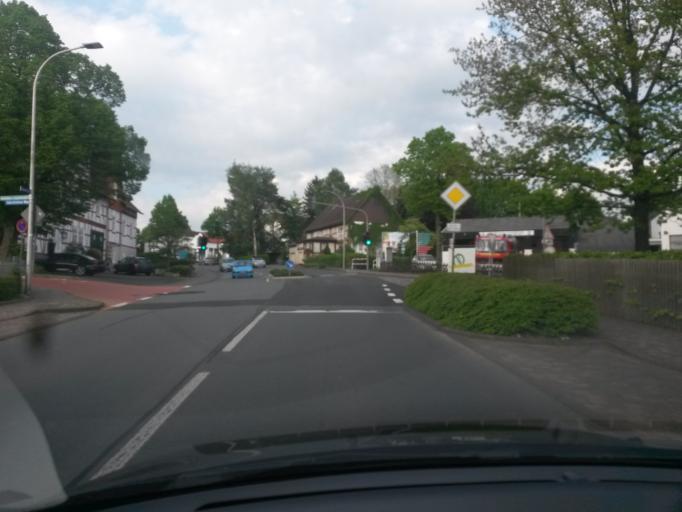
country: DE
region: Hesse
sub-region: Regierungsbezirk Kassel
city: Zierenberg
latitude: 51.3256
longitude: 9.3095
